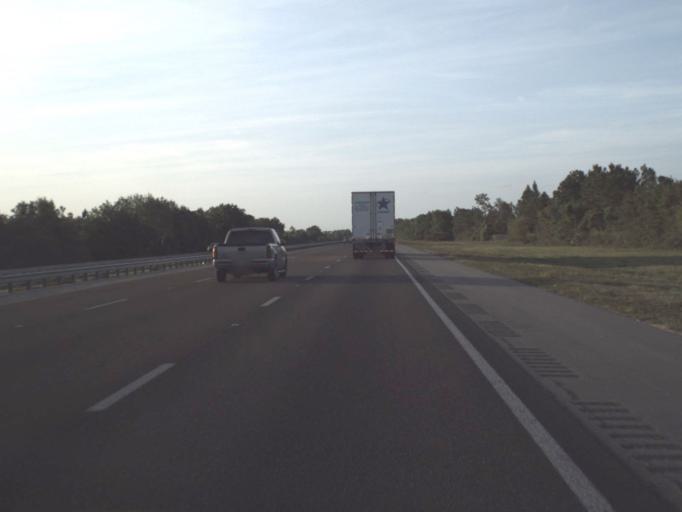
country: US
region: Florida
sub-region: Brevard County
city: Mims
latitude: 28.7423
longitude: -80.8856
